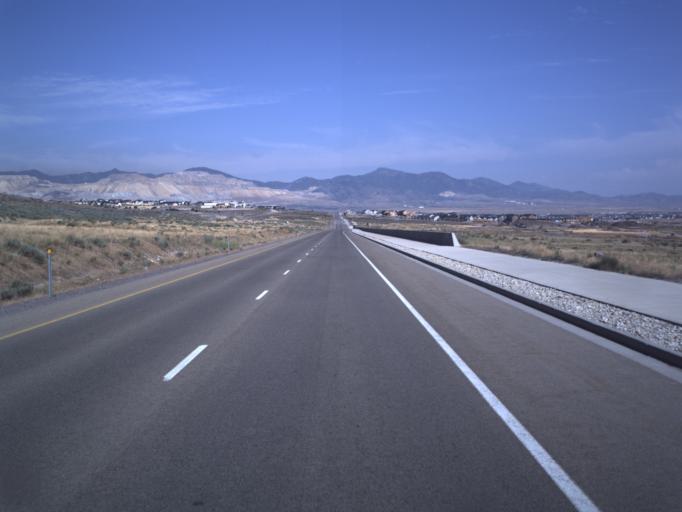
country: US
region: Utah
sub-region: Salt Lake County
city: Bluffdale
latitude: 40.4766
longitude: -111.9785
